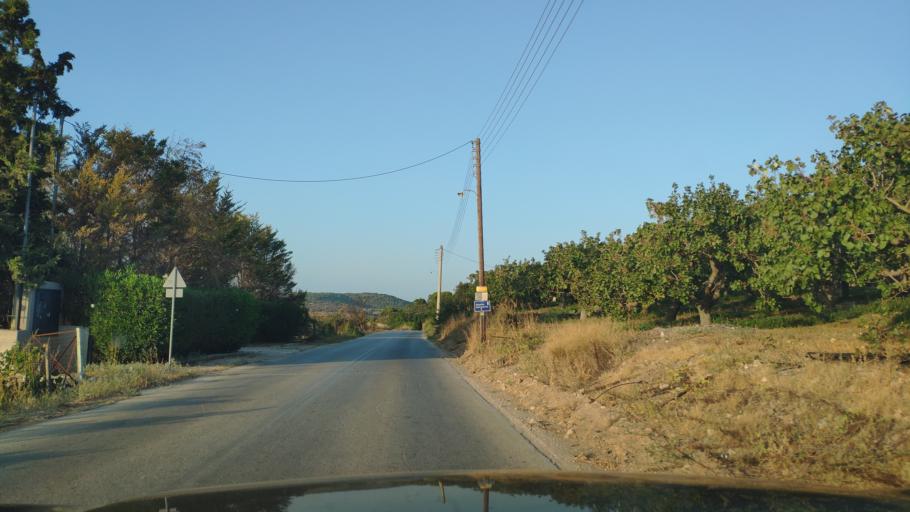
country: GR
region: Attica
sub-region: Nomarchia Anatolikis Attikis
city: Limin Mesoyaias
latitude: 37.9144
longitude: 23.9722
